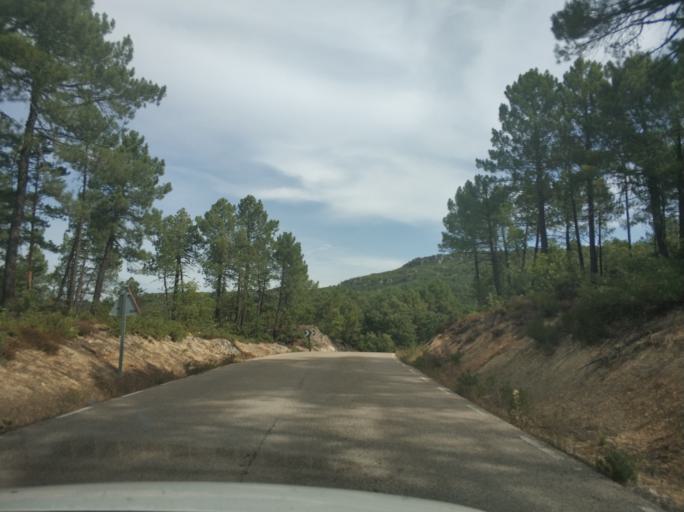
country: ES
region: Castille and Leon
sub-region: Provincia de Soria
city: Duruelo de la Sierra
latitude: 41.8962
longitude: -2.9437
